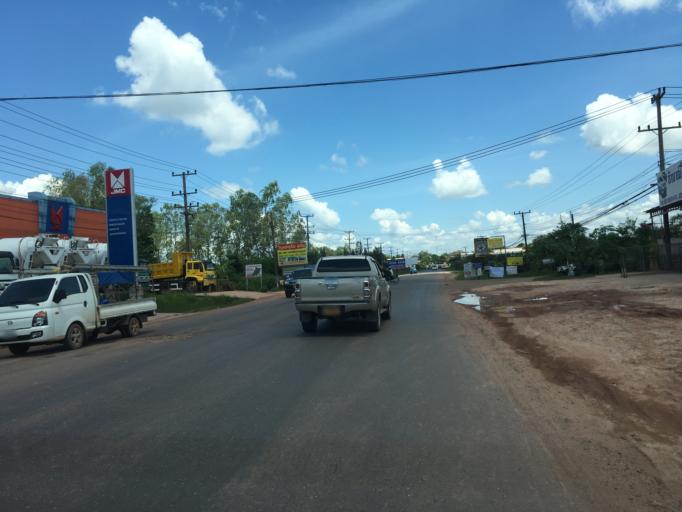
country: LA
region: Vientiane
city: Vientiane
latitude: 18.0583
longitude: 102.5397
